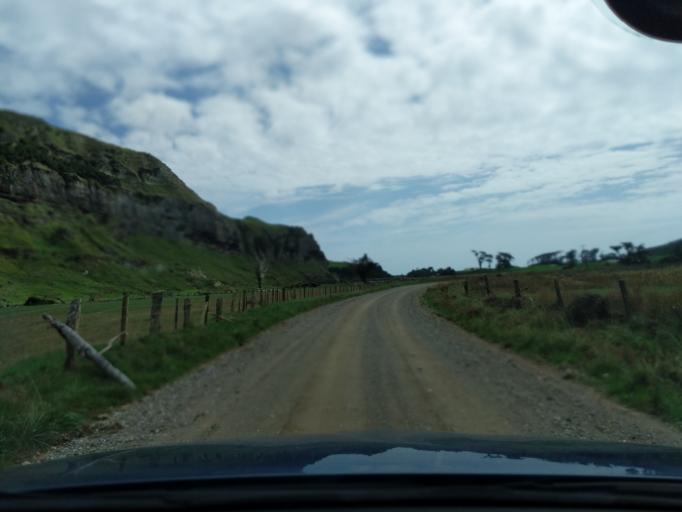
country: NZ
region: Tasman
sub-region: Tasman District
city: Takaka
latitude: -40.6497
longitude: 172.4395
